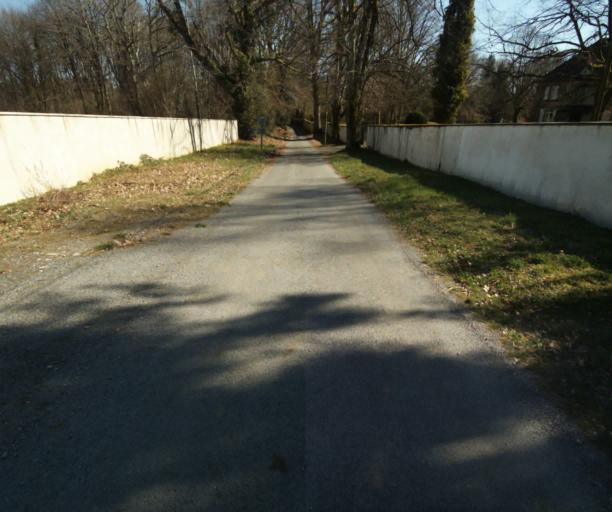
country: FR
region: Limousin
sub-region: Departement de la Correze
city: Chamboulive
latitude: 45.4662
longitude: 1.7462
